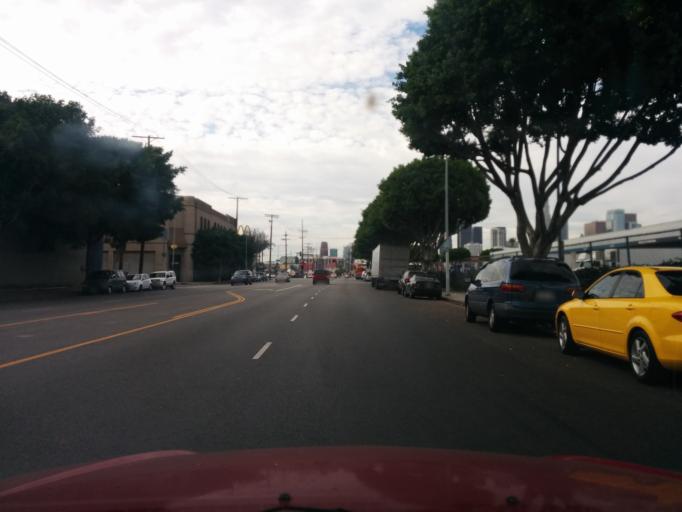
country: US
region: California
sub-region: Los Angeles County
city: Los Angeles
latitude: 34.0308
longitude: -118.2427
